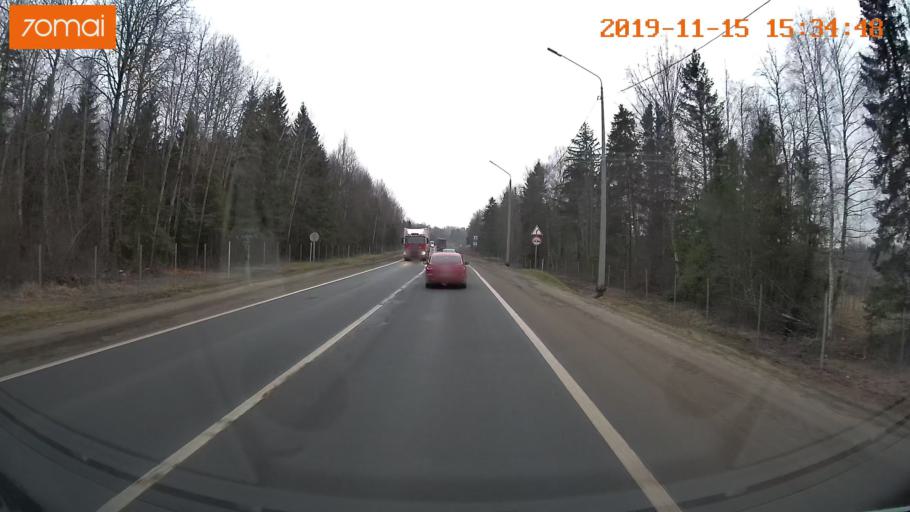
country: RU
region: Jaroslavl
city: Danilov
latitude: 58.0655
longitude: 40.0881
